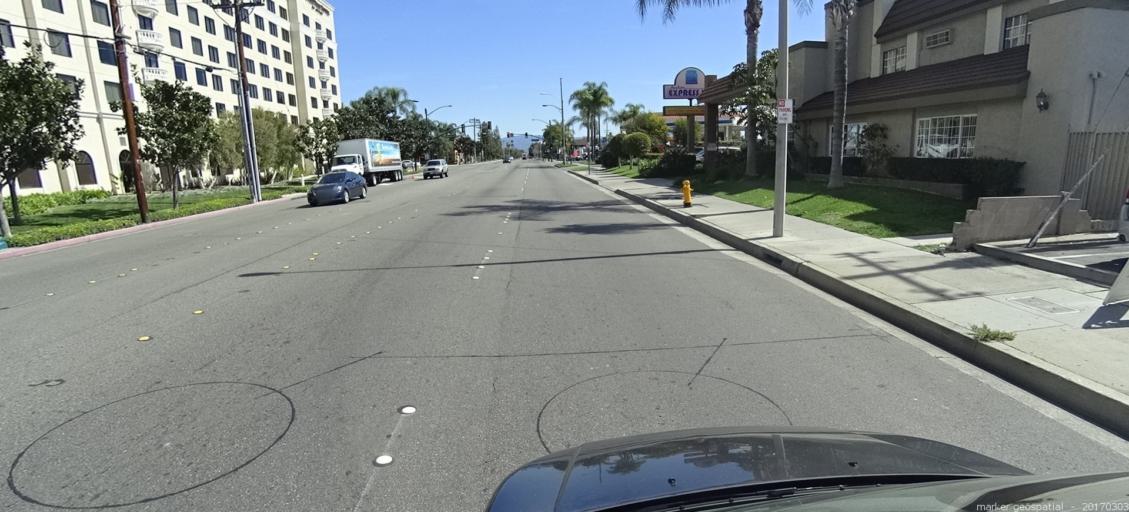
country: US
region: California
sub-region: Orange County
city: Garden Grove
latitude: 33.7960
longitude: -117.9164
